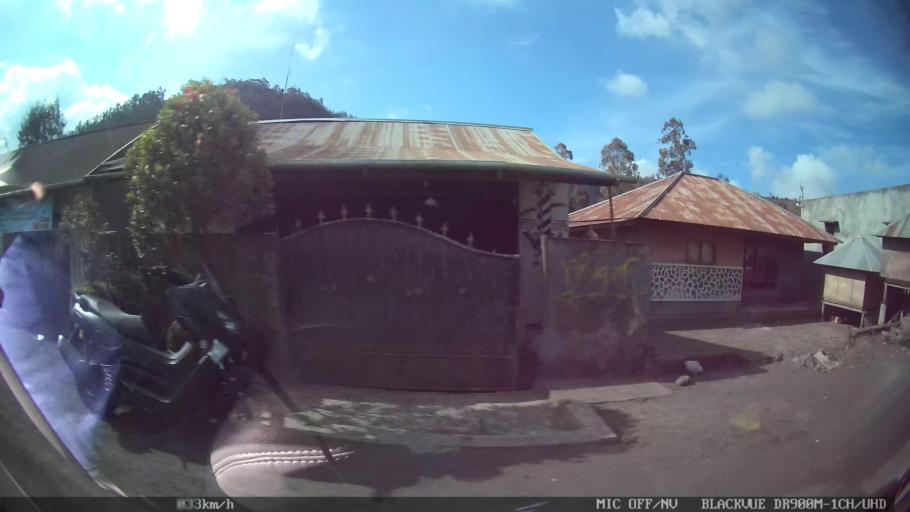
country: ID
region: Bali
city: Banjar Trunyan
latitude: -8.2156
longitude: 115.3781
